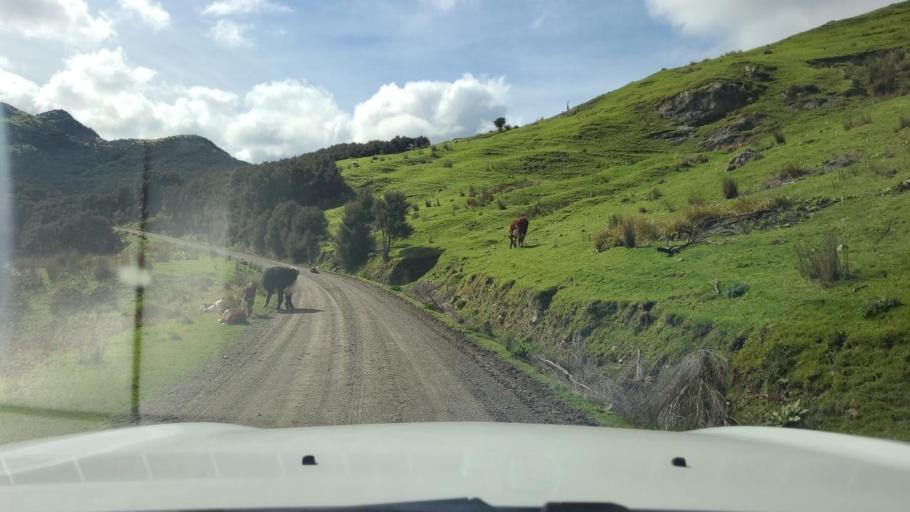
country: NZ
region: Wellington
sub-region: South Wairarapa District
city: Waipawa
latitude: -41.3609
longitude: 175.7003
